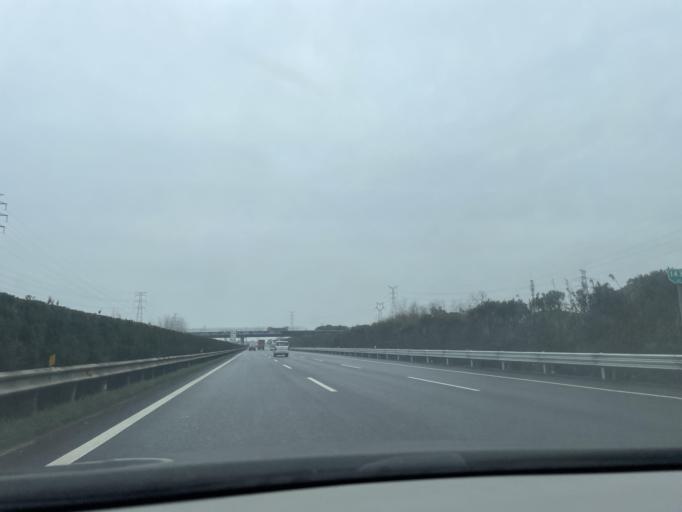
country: CN
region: Zhejiang Sheng
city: Shengshan
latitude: 30.2718
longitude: 121.3316
